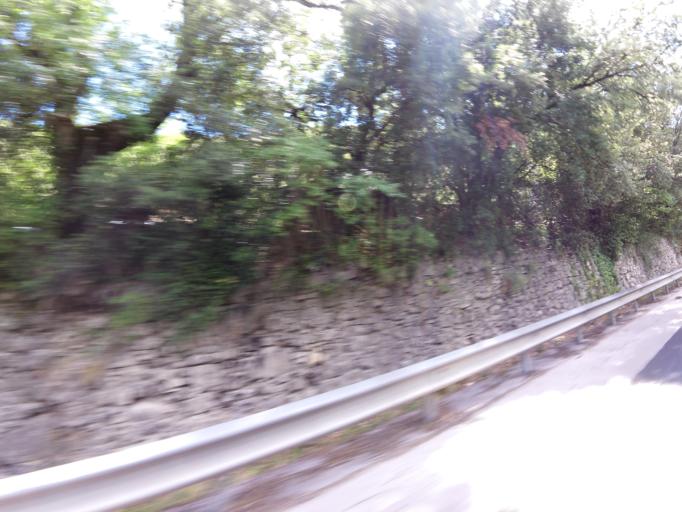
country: FR
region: Languedoc-Roussillon
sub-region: Departement de l'Herault
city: Ganges
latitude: 43.9506
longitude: 3.6851
